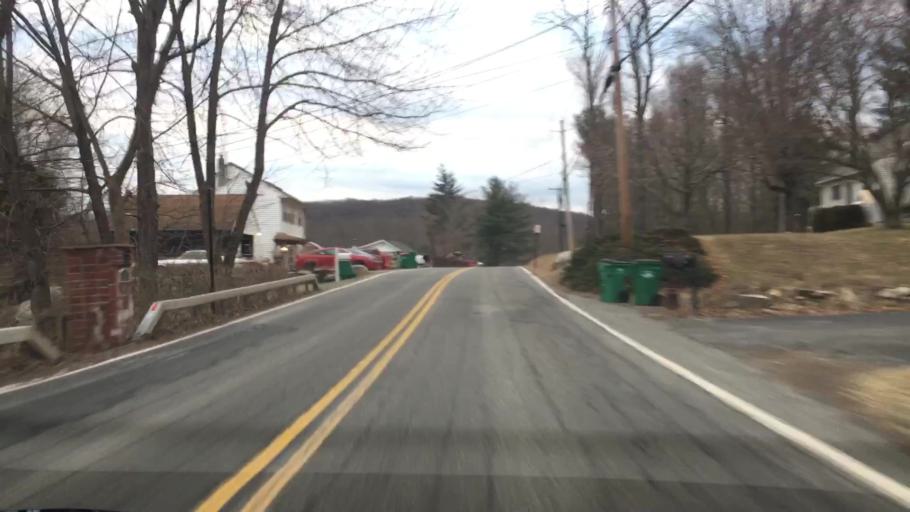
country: US
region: New York
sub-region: Putnam County
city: Lake Carmel
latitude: 41.5064
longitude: -73.6751
